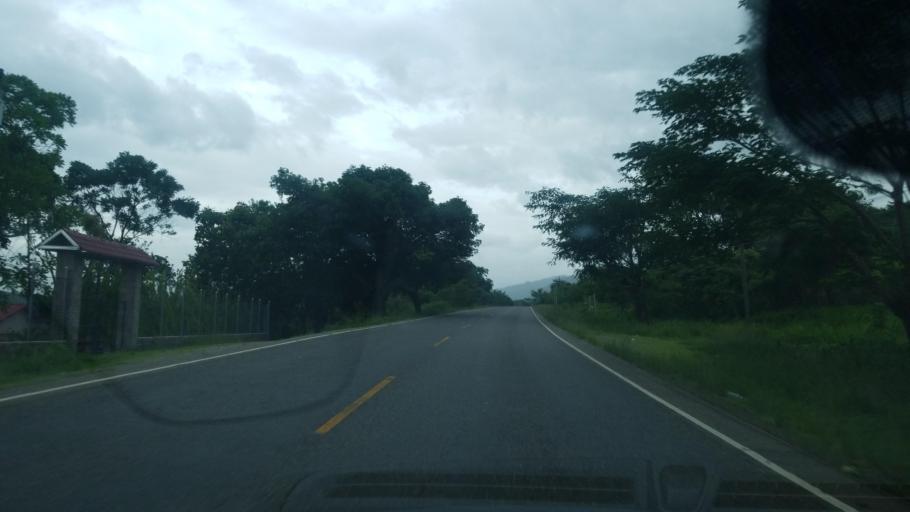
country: HN
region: Ocotepeque
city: Antigua Ocotepeque
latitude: 14.3870
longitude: -89.2065
